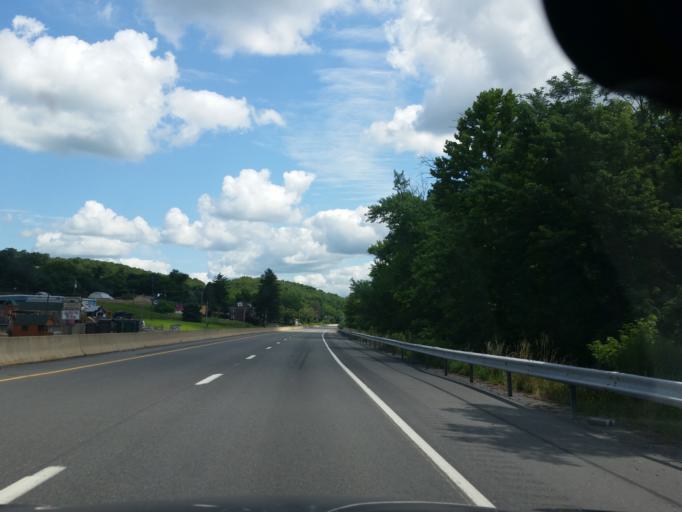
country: US
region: Pennsylvania
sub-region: Dauphin County
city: Millersburg
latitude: 40.6667
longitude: -76.9134
